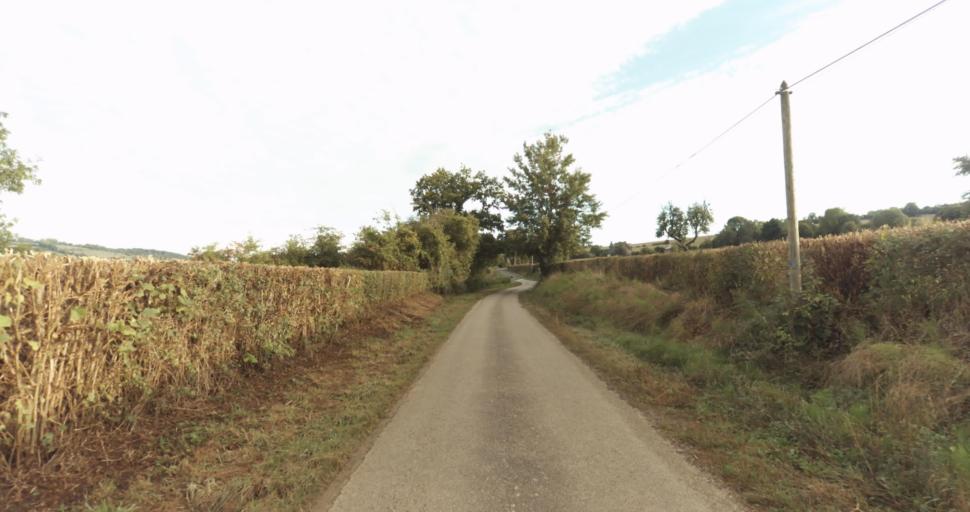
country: FR
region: Lower Normandy
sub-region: Departement de l'Orne
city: Vimoutiers
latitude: 48.9044
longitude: 0.2153
